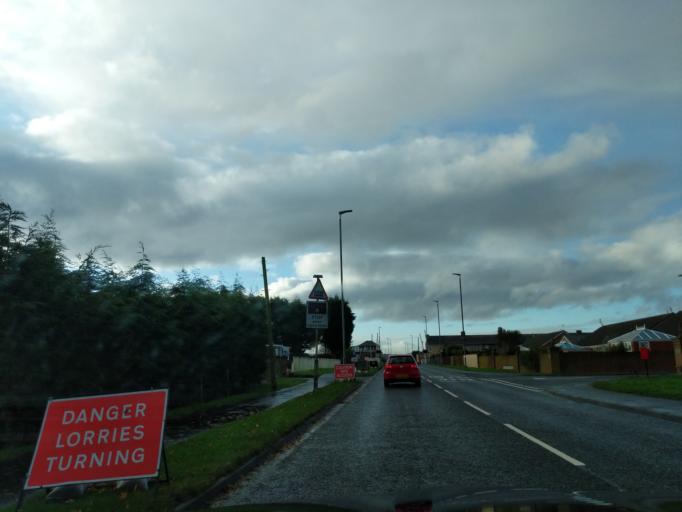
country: GB
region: England
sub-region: Northumberland
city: Blyth
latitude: 55.1040
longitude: -1.5226
